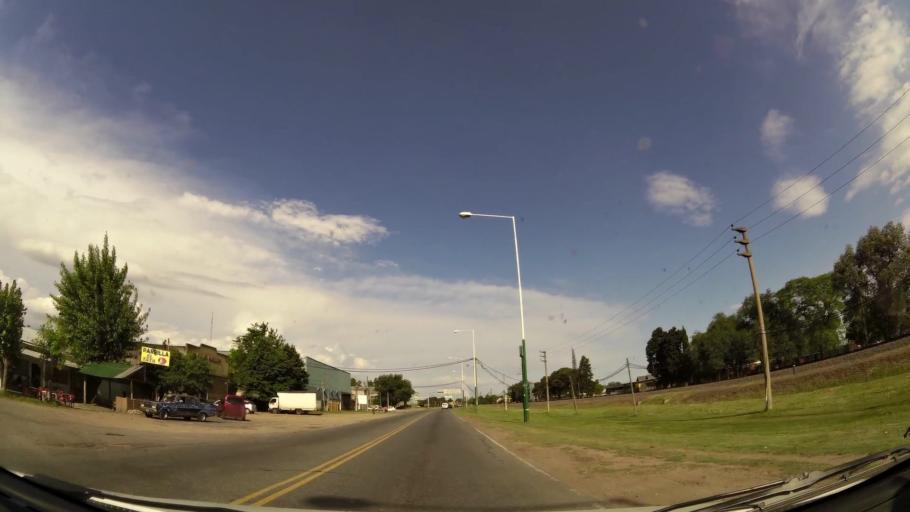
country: AR
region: Buenos Aires
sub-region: Partido de Merlo
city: Merlo
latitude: -34.6619
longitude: -58.7435
